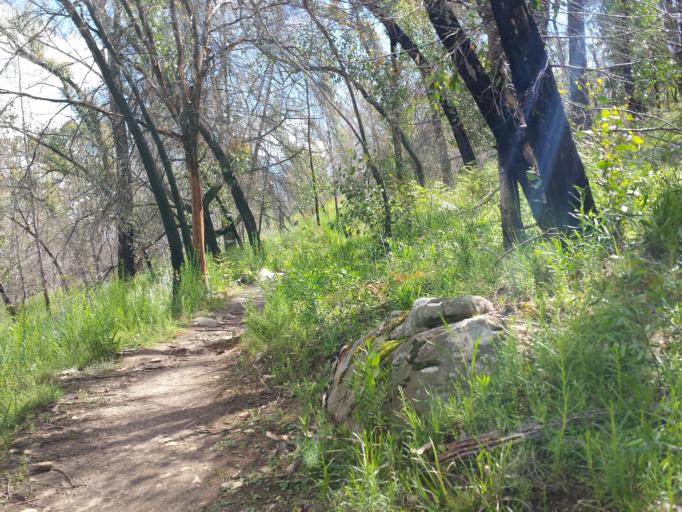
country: AU
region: Victoria
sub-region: Northern Grampians
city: Stawell
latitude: -37.2481
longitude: 142.2781
